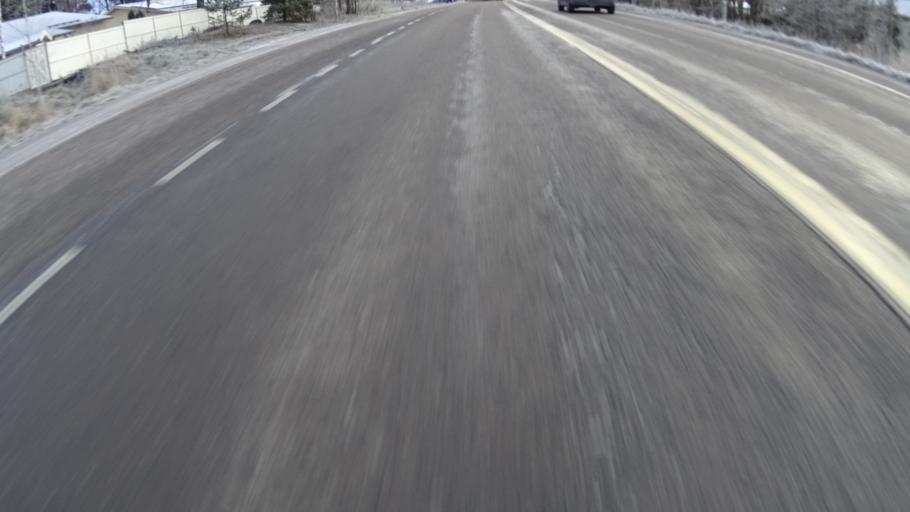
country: FI
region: Uusimaa
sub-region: Helsinki
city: Nurmijaervi
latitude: 60.3974
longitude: 24.7347
